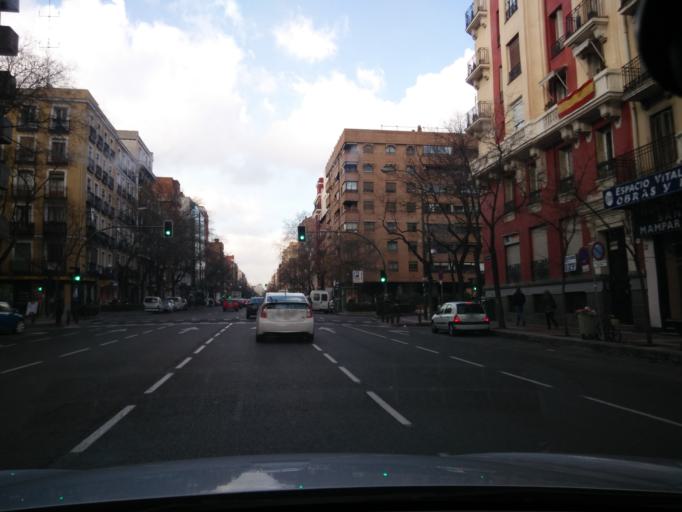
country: ES
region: Madrid
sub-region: Provincia de Madrid
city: Chamberi
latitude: 40.4331
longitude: -3.6979
